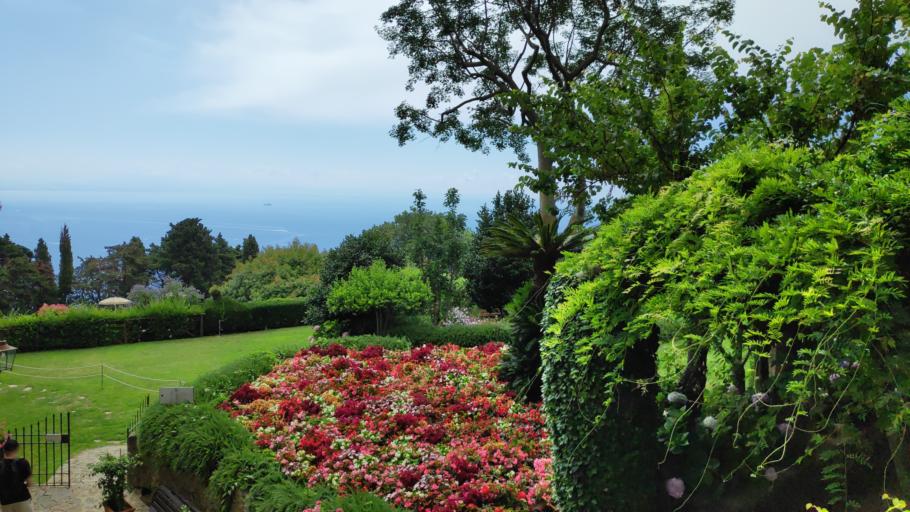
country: IT
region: Campania
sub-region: Provincia di Salerno
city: Ravello
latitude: 40.6440
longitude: 14.6109
